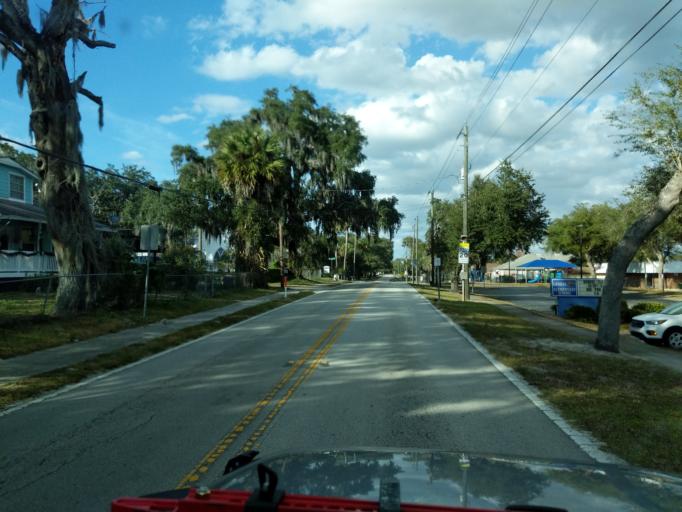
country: US
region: Florida
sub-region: Seminole County
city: Geneva
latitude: 28.7383
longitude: -81.1152
